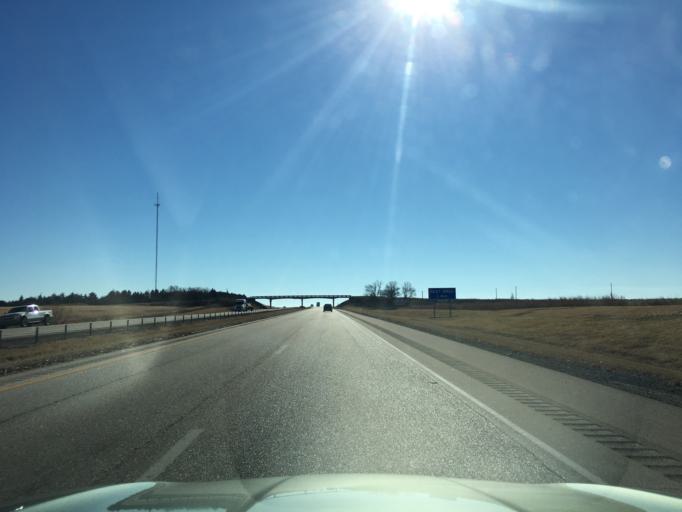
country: US
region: Oklahoma
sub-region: Kay County
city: Blackwell
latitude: 36.8724
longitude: -97.3495
